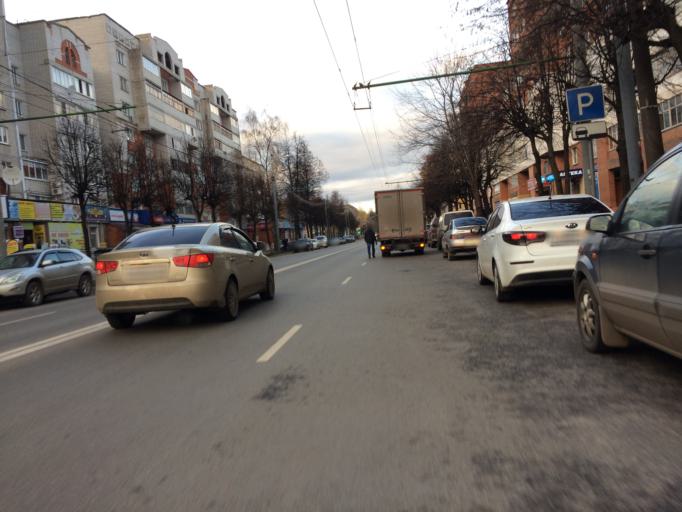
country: RU
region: Mariy-El
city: Yoshkar-Ola
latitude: 56.6423
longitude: 47.8899
